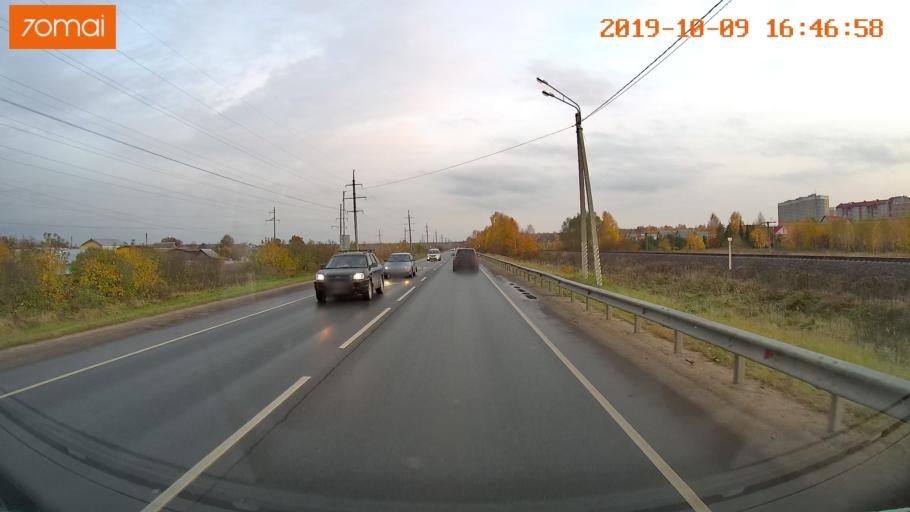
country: RU
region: Kostroma
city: Volgorechensk
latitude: 57.4400
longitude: 41.1710
